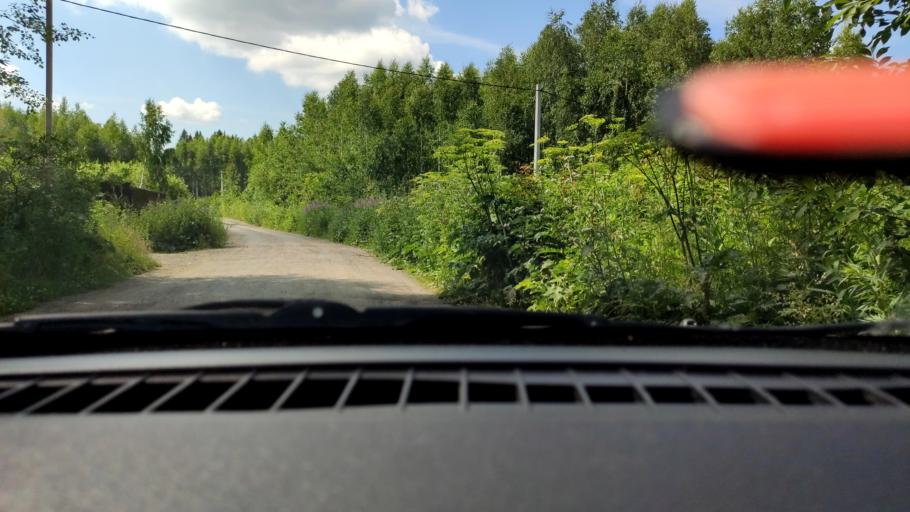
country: RU
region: Perm
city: Perm
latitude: 58.1503
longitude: 56.2978
